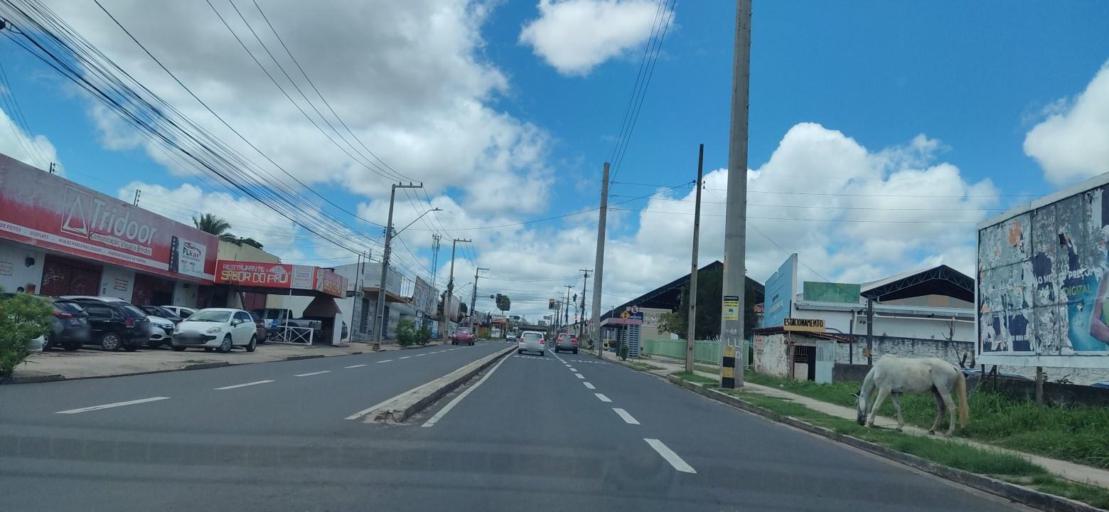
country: BR
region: Piaui
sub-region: Teresina
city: Teresina
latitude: -5.0876
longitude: -42.7646
